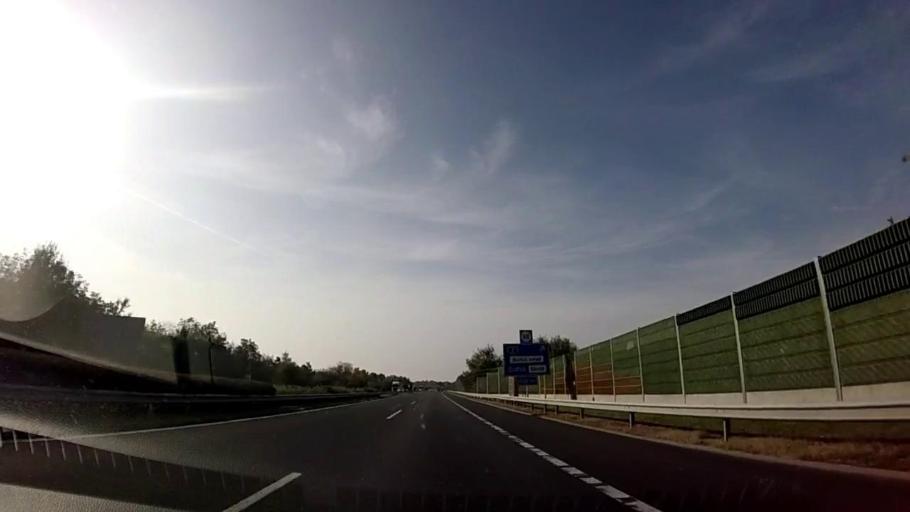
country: HU
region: Somogy
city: Balatonszabadi
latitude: 46.9412
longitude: 18.1463
